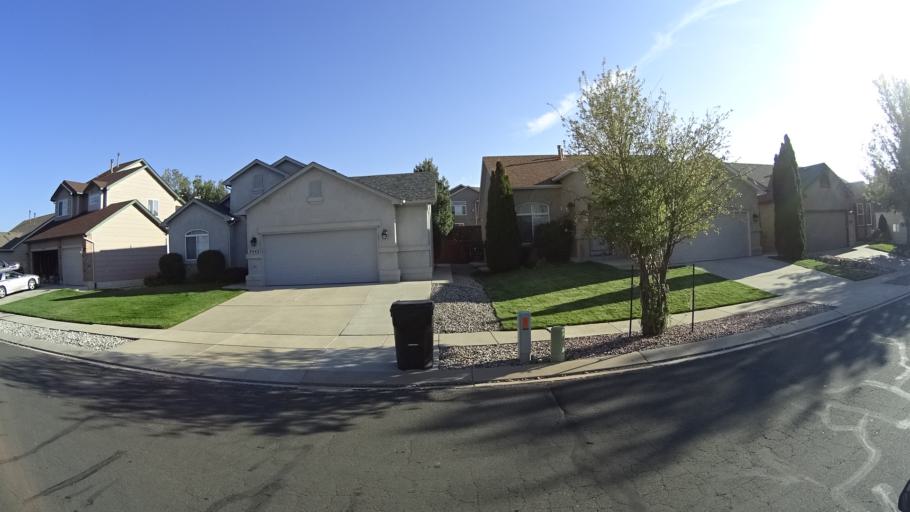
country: US
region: Colorado
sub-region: El Paso County
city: Cimarron Hills
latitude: 38.8918
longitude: -104.6993
